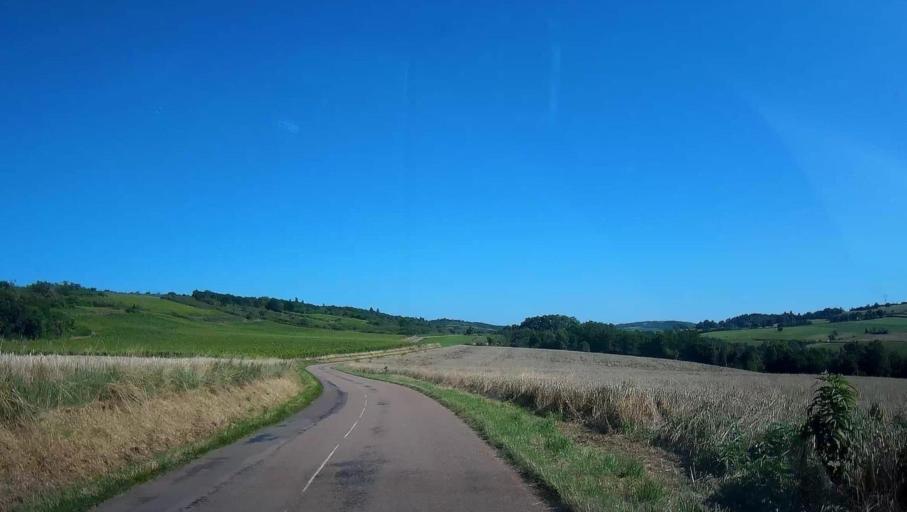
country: FR
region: Bourgogne
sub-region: Departement de Saone-et-Loire
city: Couches
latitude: 46.8961
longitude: 4.5921
